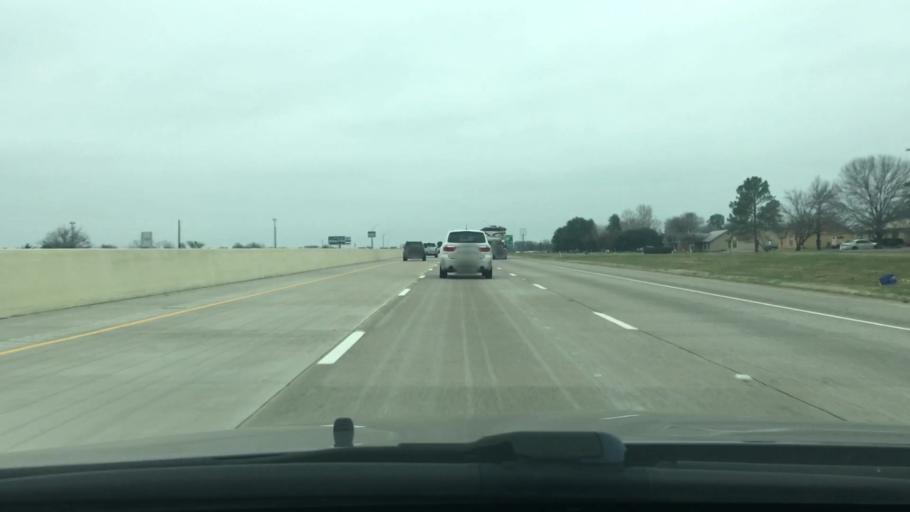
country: US
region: Texas
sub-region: Navarro County
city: Corsicana
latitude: 32.0156
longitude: -96.4370
